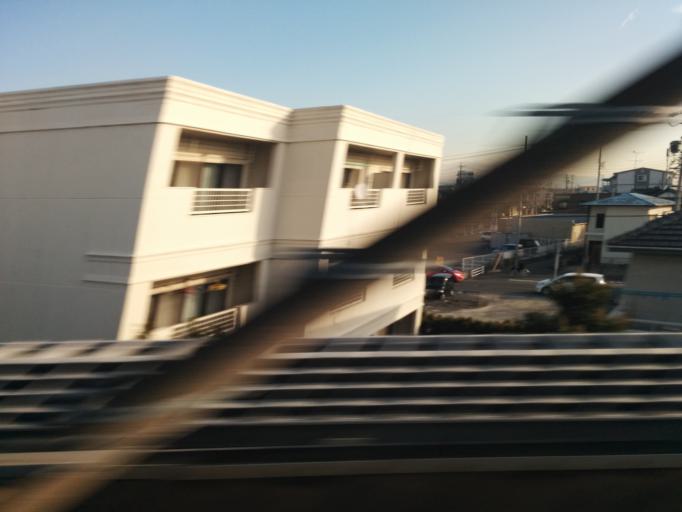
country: JP
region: Aichi
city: Chiryu
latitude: 34.9829
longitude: 137.0473
